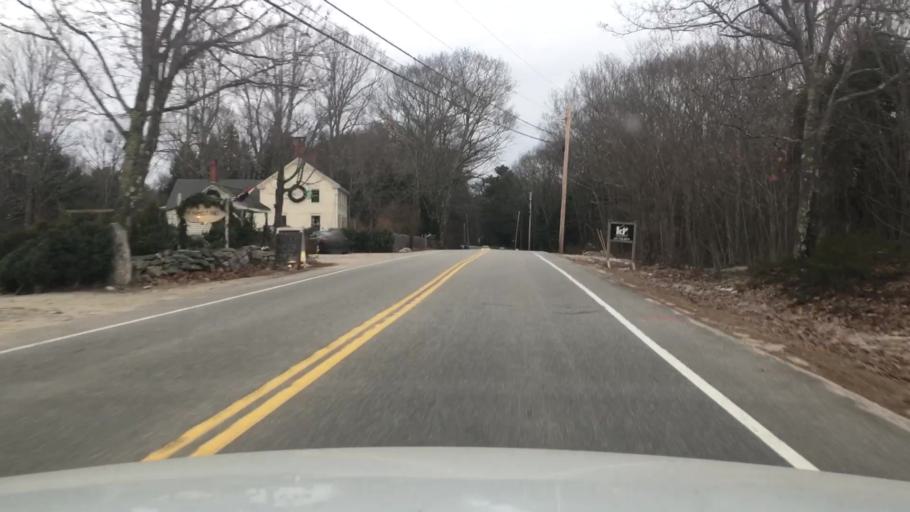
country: US
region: Maine
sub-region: Cumberland County
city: Freeport
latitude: 43.8620
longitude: -70.0726
